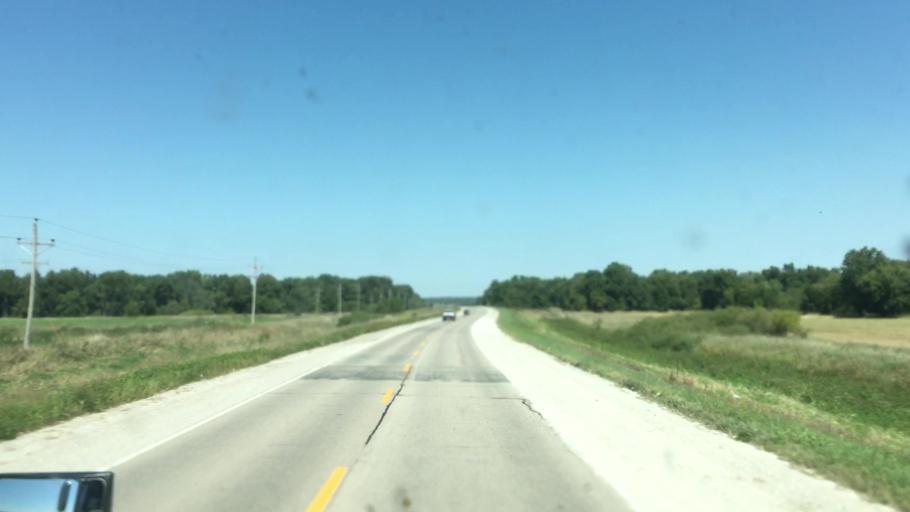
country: US
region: Iowa
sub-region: Benton County
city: Belle Plaine
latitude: 41.8546
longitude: -92.2783
